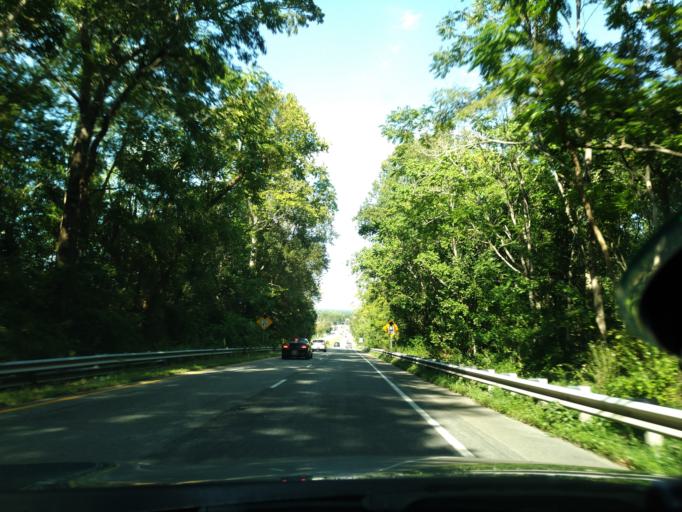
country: US
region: Virginia
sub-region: King George County
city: King George
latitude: 38.1580
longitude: -77.2050
